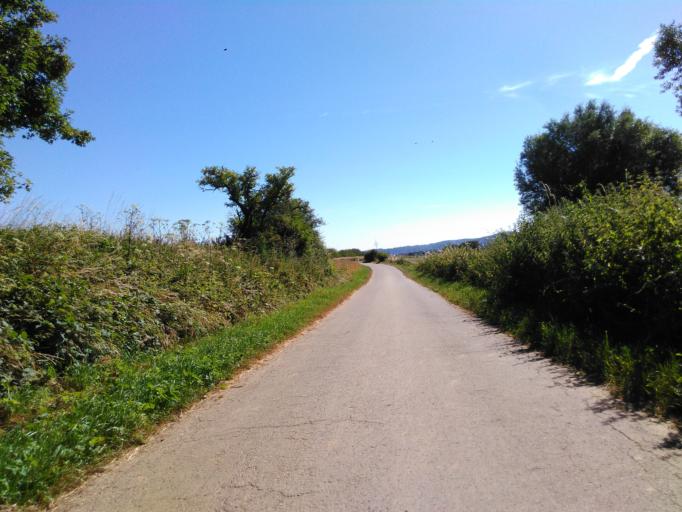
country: LU
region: Luxembourg
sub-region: Canton d'Esch-sur-Alzette
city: Sanem
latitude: 49.5555
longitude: 5.9502
